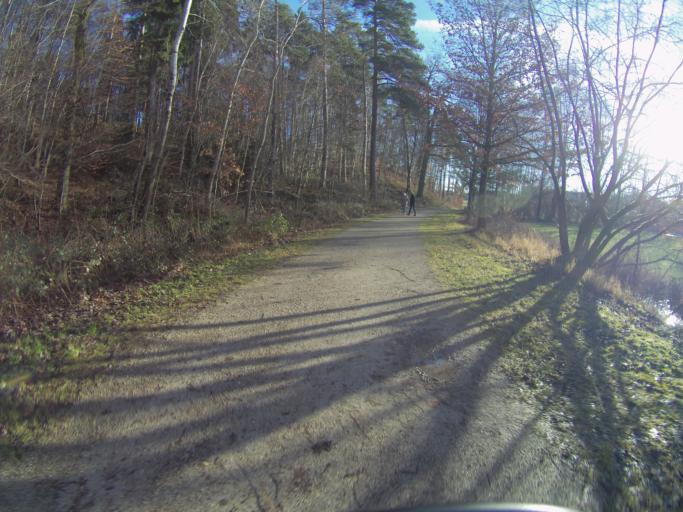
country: DE
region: Bavaria
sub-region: Upper Bavaria
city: Freising
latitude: 48.4164
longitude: 11.7549
